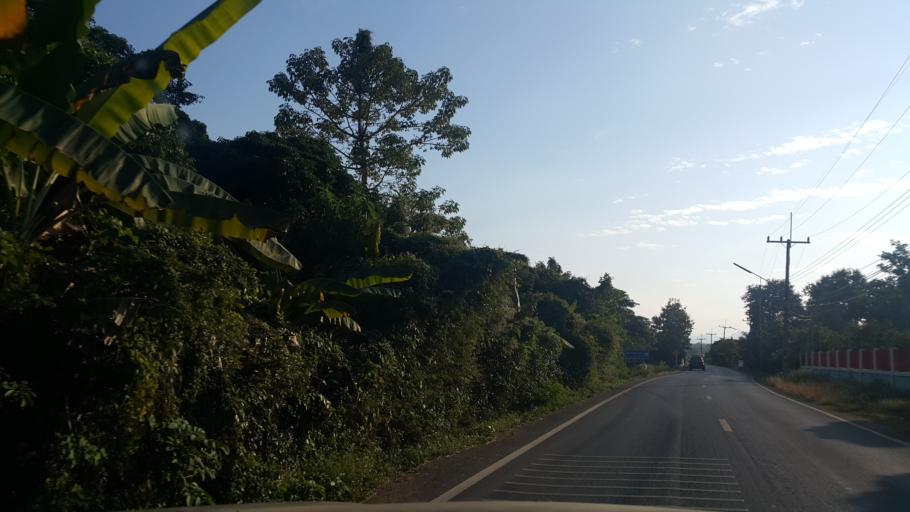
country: TH
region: Lampang
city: Ko Kha
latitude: 18.1062
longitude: 99.3395
